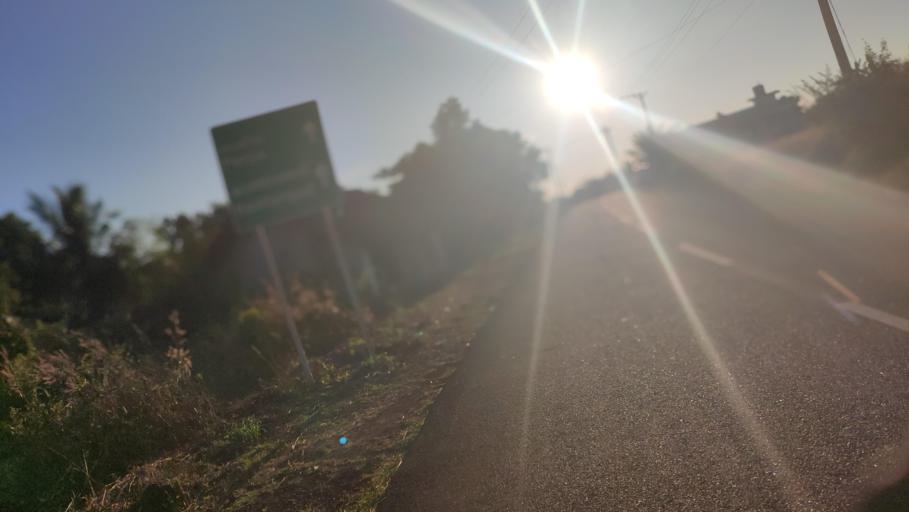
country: IN
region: Kerala
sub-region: Kasaragod District
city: Kasaragod
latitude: 12.4561
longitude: 75.0976
